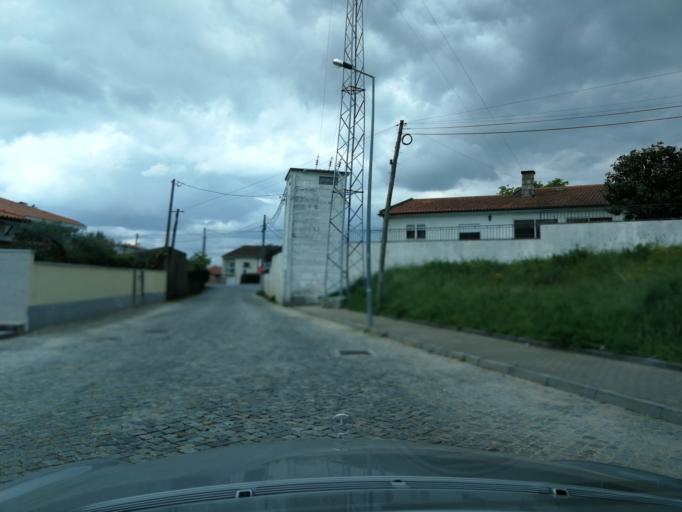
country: PT
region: Braga
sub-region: Braga
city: Braga
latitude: 41.5320
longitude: -8.3957
